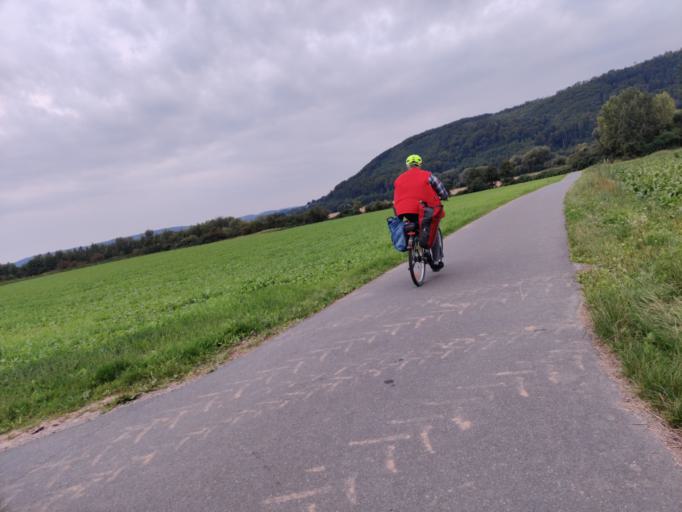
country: DE
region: Lower Saxony
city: Holzminden
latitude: 51.8486
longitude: 9.4579
